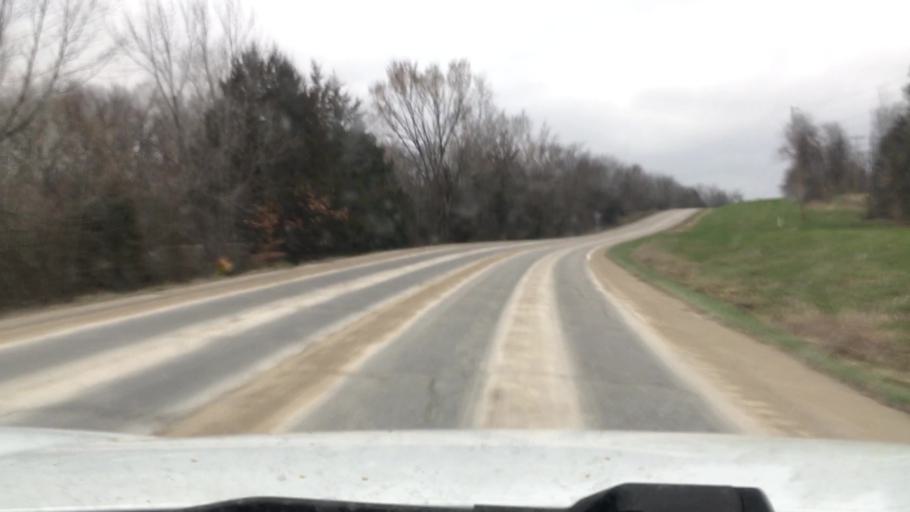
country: US
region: Missouri
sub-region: Saint Charles County
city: Weldon Spring
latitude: 38.6731
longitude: -90.7332
